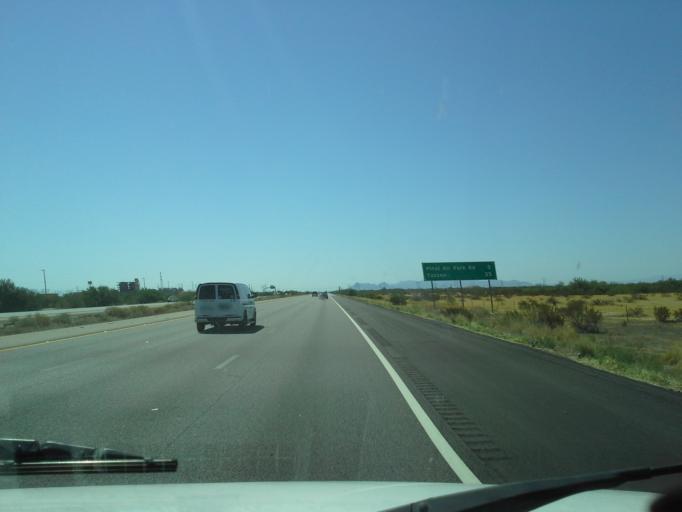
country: US
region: Arizona
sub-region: Pima County
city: Avra Valley
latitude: 32.5626
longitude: -111.3143
